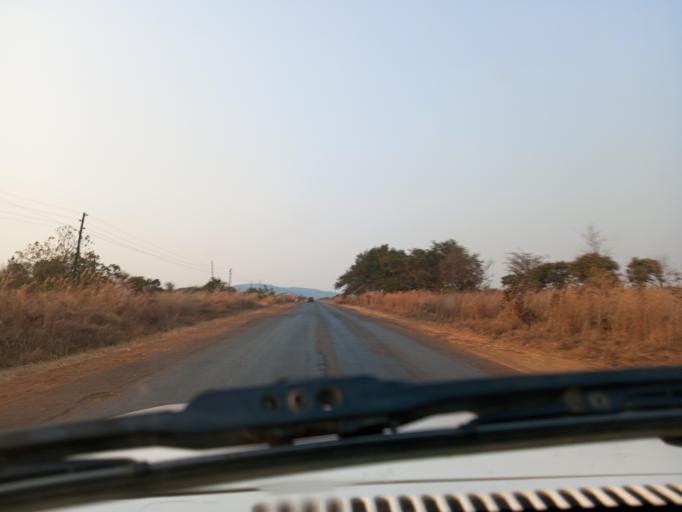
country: ZM
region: Northern
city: Mpika
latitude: -11.9088
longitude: 31.4147
